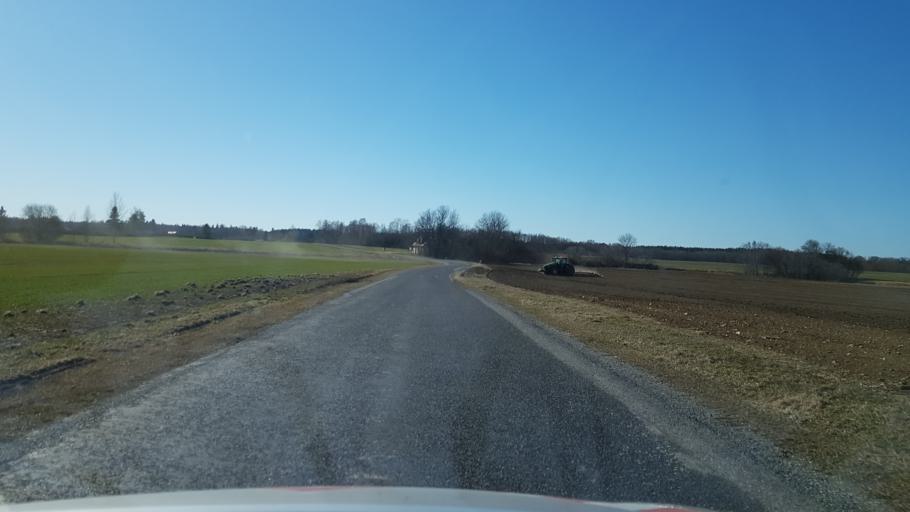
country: EE
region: Laeaene-Virumaa
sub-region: Kadrina vald
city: Kadrina
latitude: 59.4433
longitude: 26.1144
